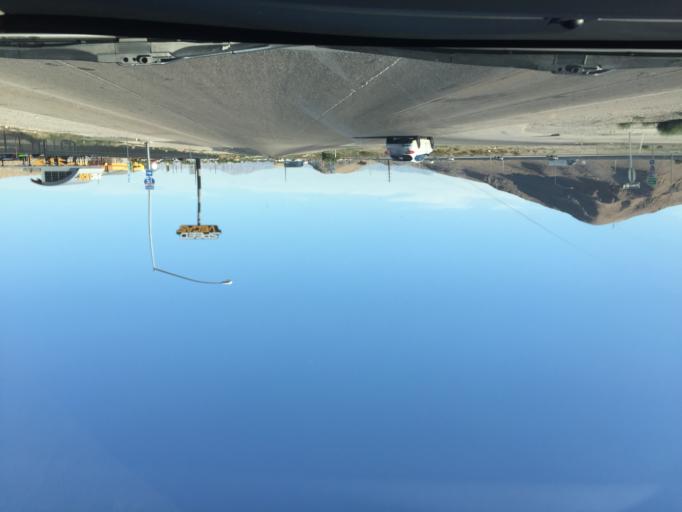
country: US
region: Nevada
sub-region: Clark County
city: Enterprise
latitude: 35.9316
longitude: -115.1909
